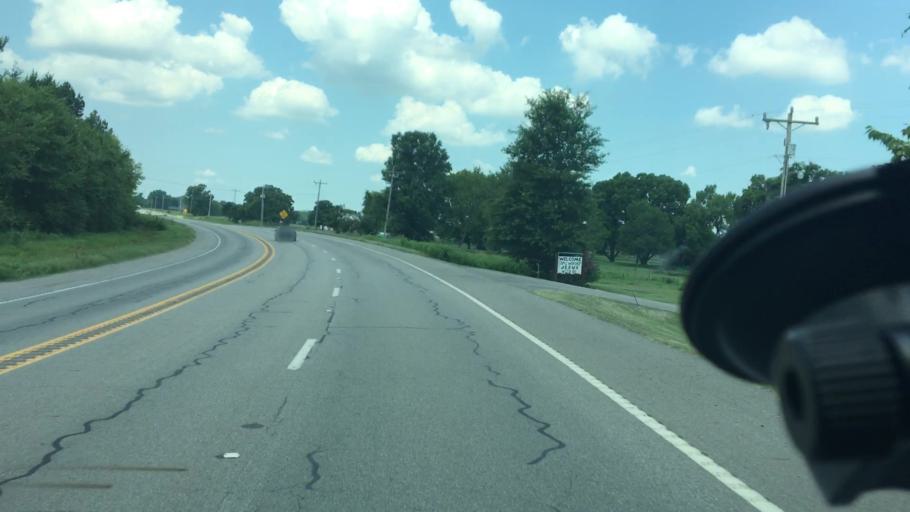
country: US
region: Arkansas
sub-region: Logan County
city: Paris
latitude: 35.2983
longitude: -93.8121
